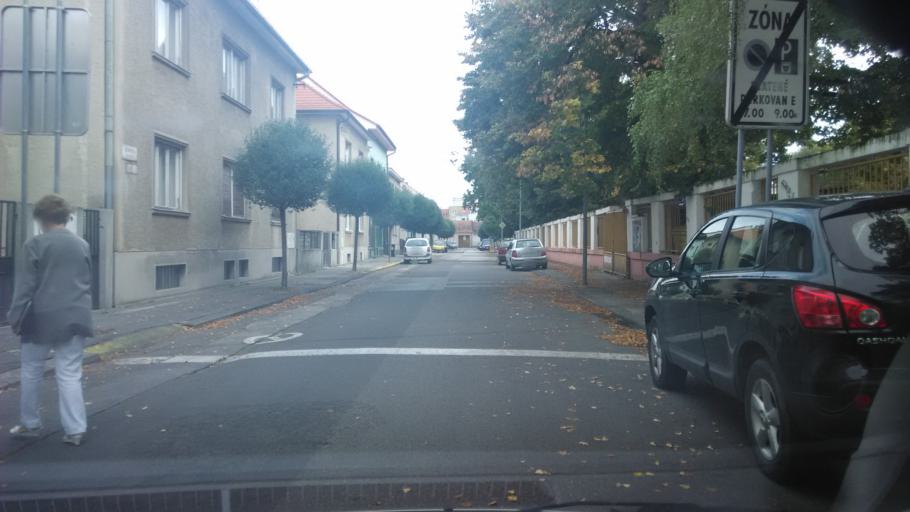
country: SK
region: Trnavsky
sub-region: Okres Trnava
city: Piestany
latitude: 48.5925
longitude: 17.8308
